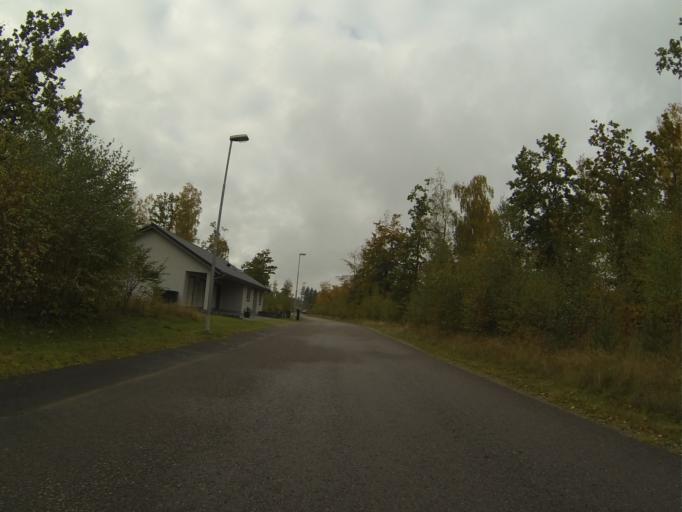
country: SE
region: Skane
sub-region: Sjobo Kommun
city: Sjoebo
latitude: 55.6374
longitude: 13.6765
